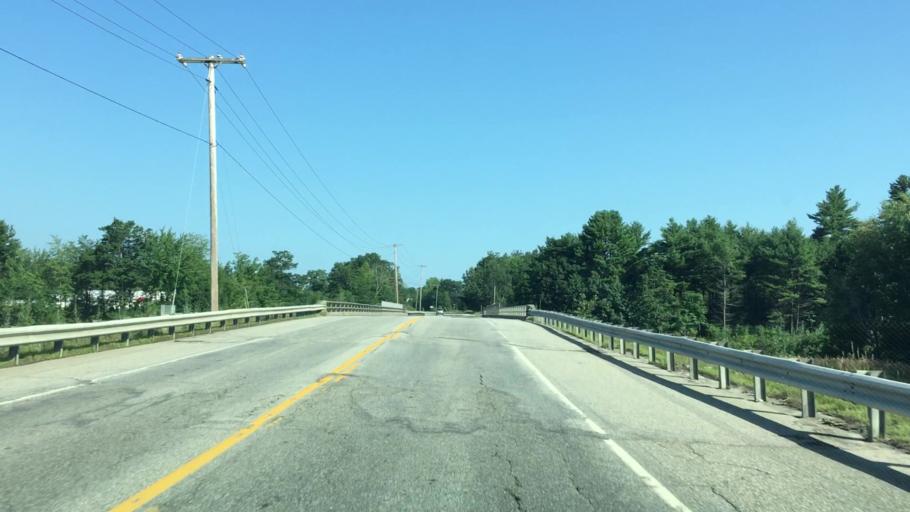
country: US
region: Maine
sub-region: Androscoggin County
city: Minot
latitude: 44.0352
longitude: -70.2729
